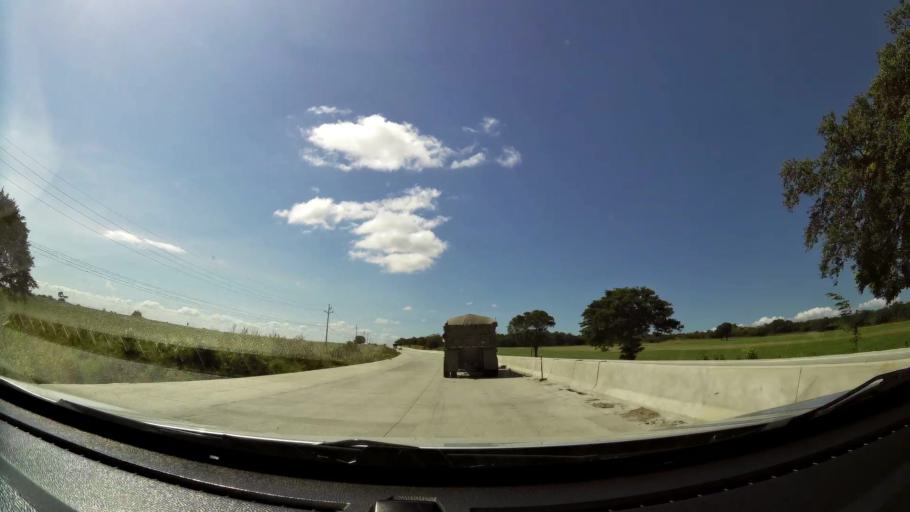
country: CR
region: Guanacaste
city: Bagaces
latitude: 10.5406
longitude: -85.3201
